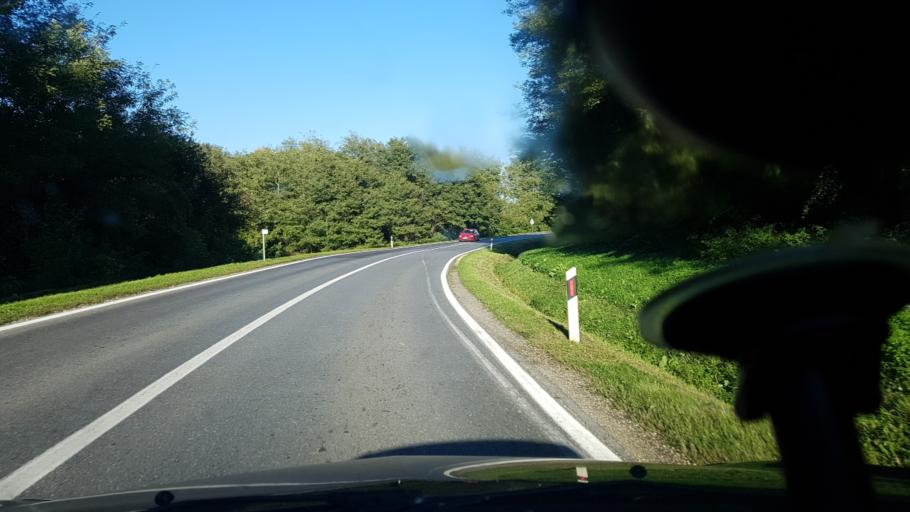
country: HR
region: Koprivnicko-Krizevacka
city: Virje
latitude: 46.0223
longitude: 16.9744
